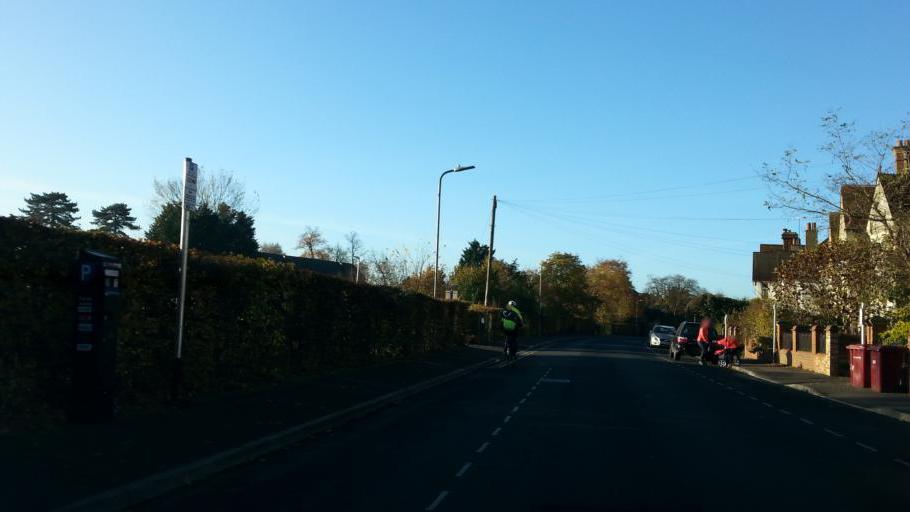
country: GB
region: England
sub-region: Reading
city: Reading
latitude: 51.4438
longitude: -0.9520
